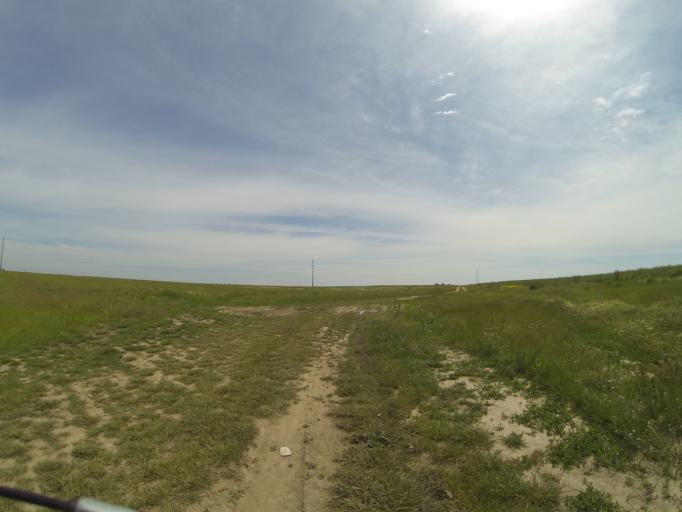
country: RO
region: Dolj
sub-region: Comuna Ghindeni
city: Ghindeni
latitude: 44.2073
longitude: 23.9445
